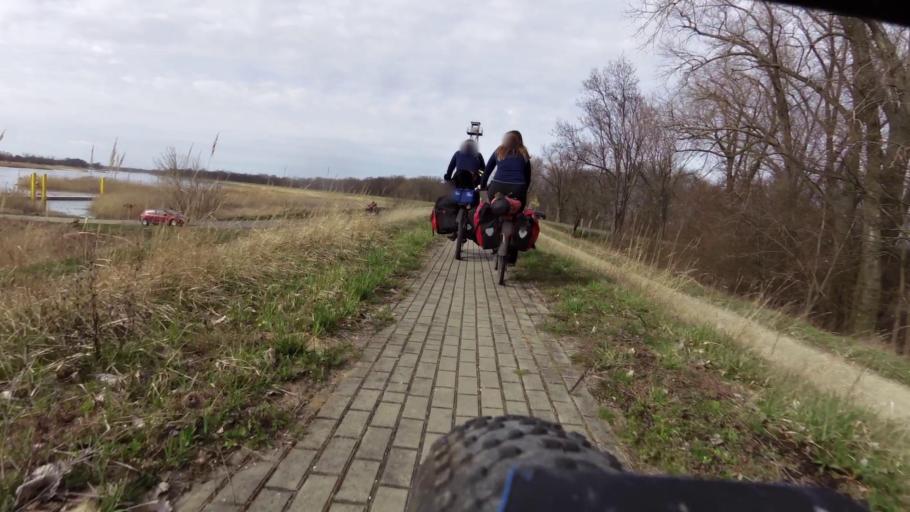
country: PL
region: Lubusz
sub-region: Powiat slubicki
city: Gorzyca
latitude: 52.4997
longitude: 14.6369
